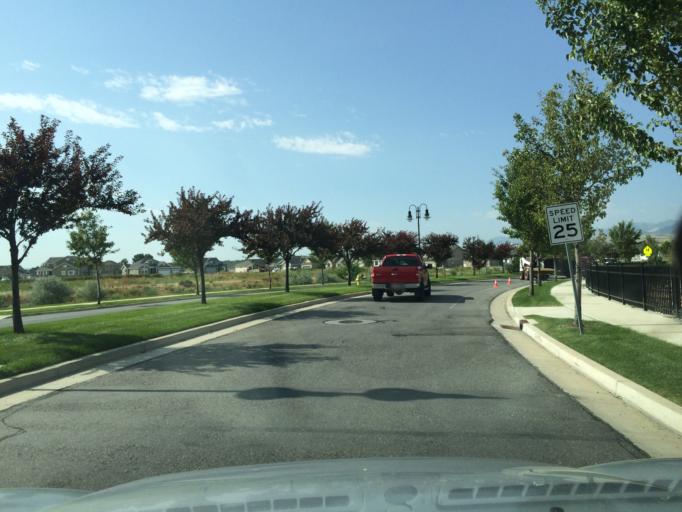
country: US
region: Utah
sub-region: Salt Lake County
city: West Valley City
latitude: 40.7118
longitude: -112.0137
